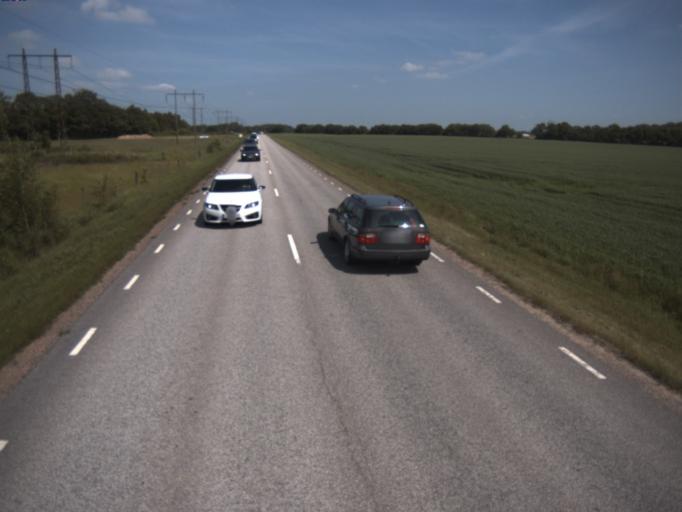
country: SE
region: Skane
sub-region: Helsingborg
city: Helsingborg
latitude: 56.0915
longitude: 12.6727
